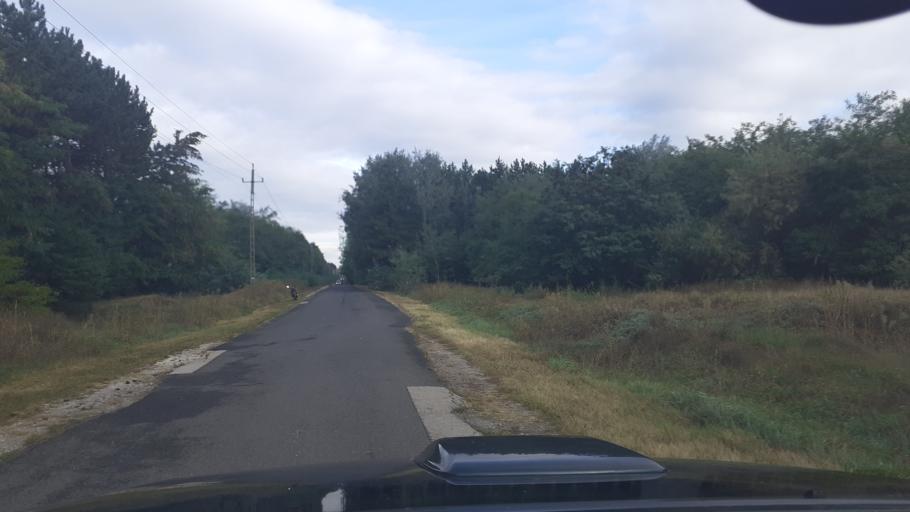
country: HU
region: Fejer
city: Baracs
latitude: 46.9404
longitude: 18.8656
